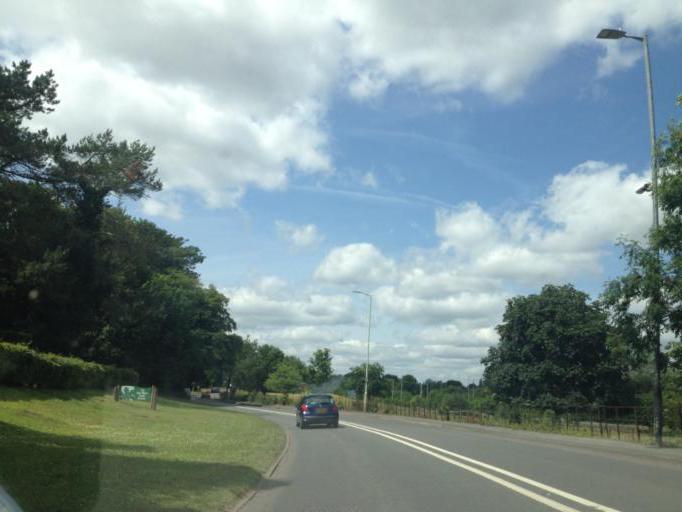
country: GB
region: England
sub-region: Hertfordshire
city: Hemel Hempstead
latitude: 51.7439
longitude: -0.5064
